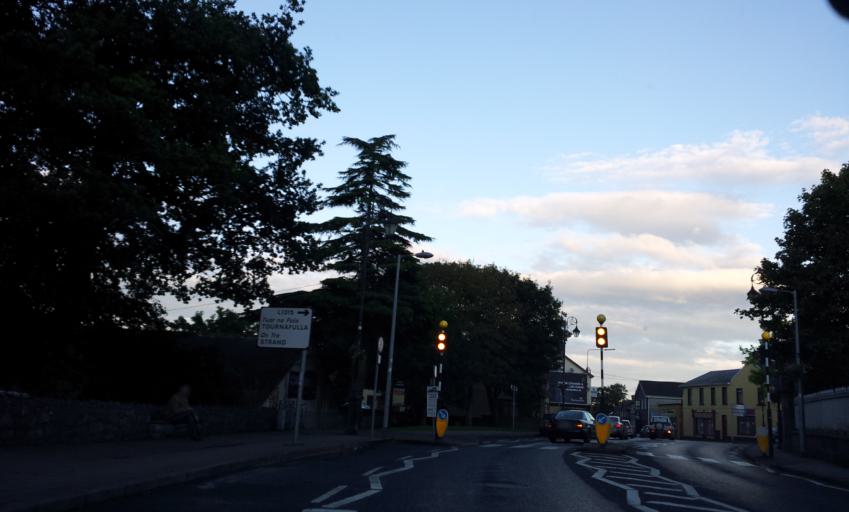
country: IE
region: Munster
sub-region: County Limerick
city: Newcastle West
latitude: 52.4495
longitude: -9.0591
